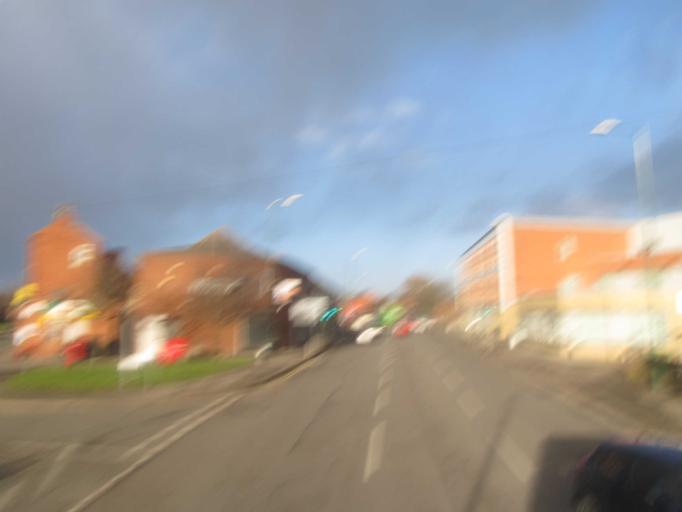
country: GB
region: England
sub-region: Nottinghamshire
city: Hucknall
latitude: 52.9973
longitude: -1.1974
